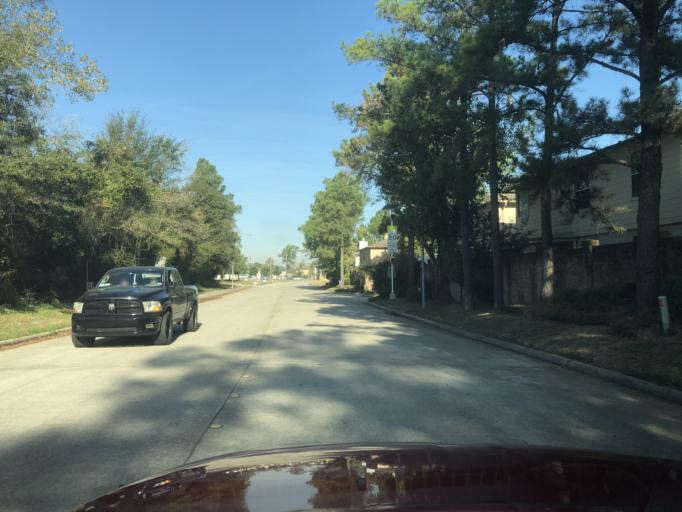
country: US
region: Texas
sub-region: Harris County
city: Spring
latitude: 30.0055
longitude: -95.4567
